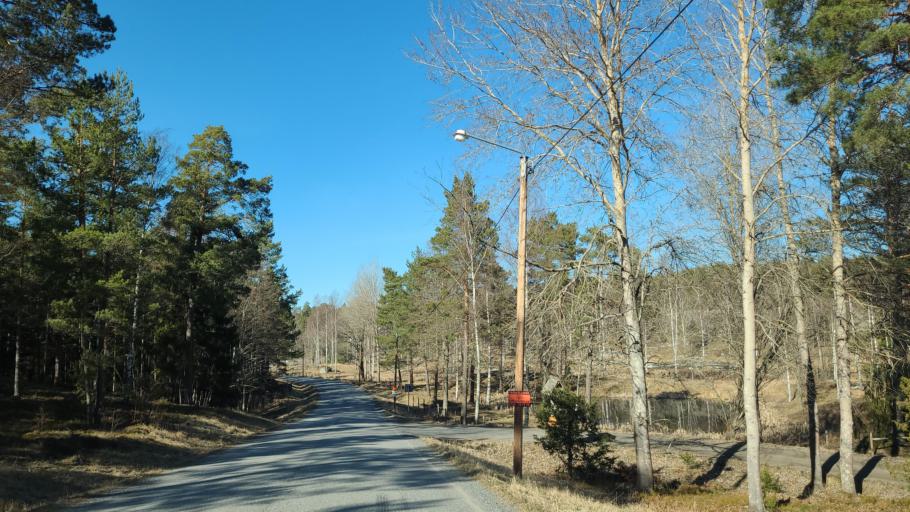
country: SE
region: Stockholm
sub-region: Varmdo Kommun
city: Hemmesta
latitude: 59.2789
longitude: 18.5696
